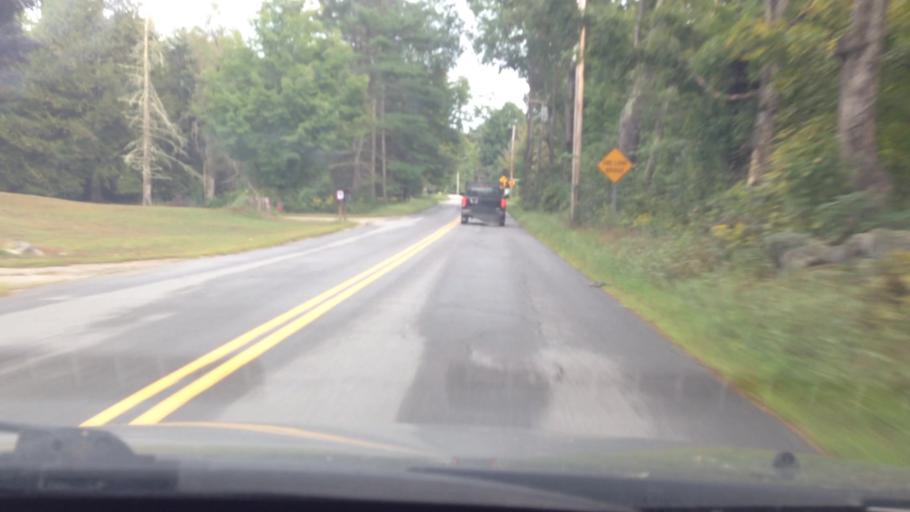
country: US
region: New Hampshire
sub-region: Cheshire County
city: Swanzey
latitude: 42.8878
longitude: -72.2898
